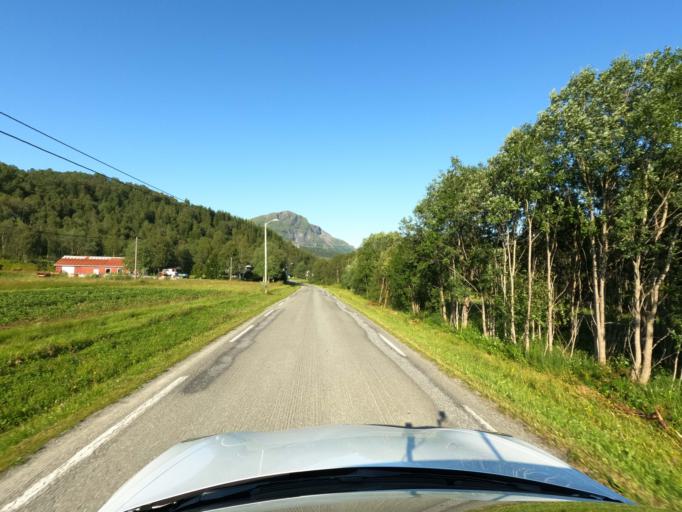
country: NO
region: Nordland
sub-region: Narvik
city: Bjerkvik
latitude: 68.5568
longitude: 17.6177
